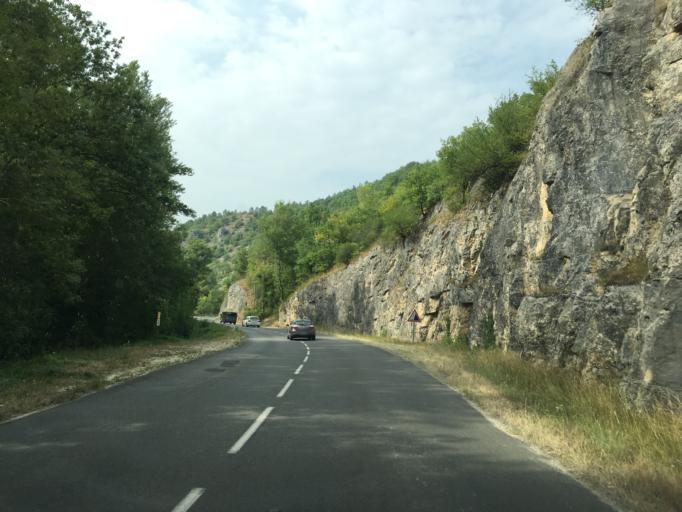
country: FR
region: Midi-Pyrenees
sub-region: Departement du Lot
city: Souillac
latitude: 44.8718
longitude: 1.4978
